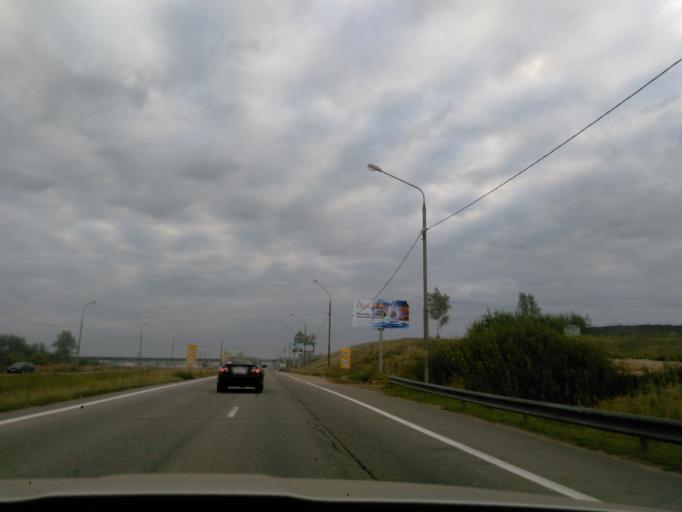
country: RU
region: Moskovskaya
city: Novopodrezkovo
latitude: 55.9684
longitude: 37.3706
